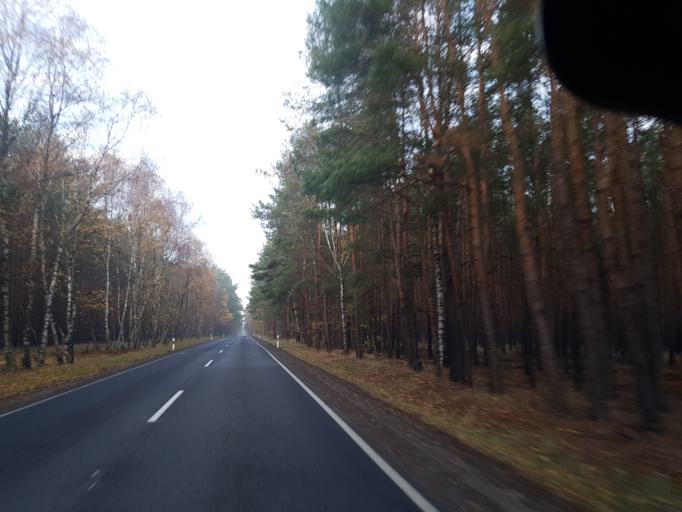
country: DE
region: Saxony-Anhalt
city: Seyda
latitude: 51.8957
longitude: 12.8636
